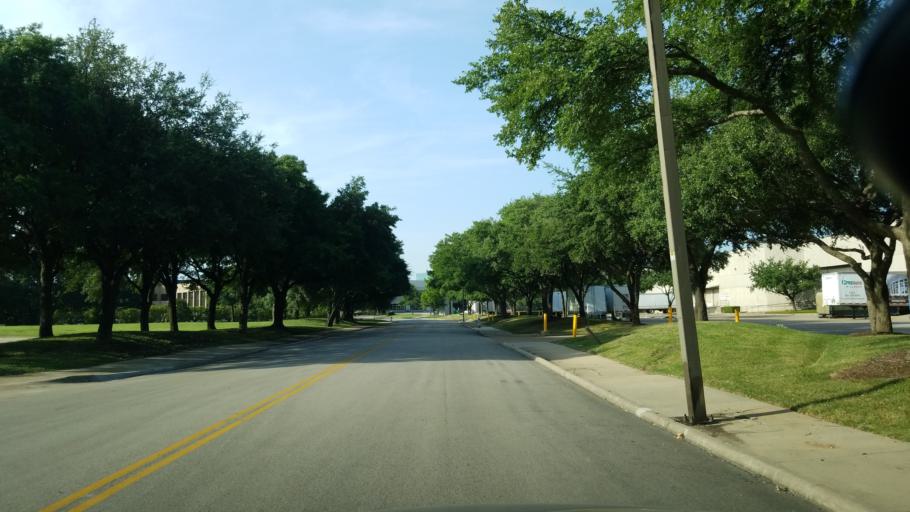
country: US
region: Texas
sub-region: Dallas County
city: Coppell
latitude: 32.9286
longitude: -97.0171
